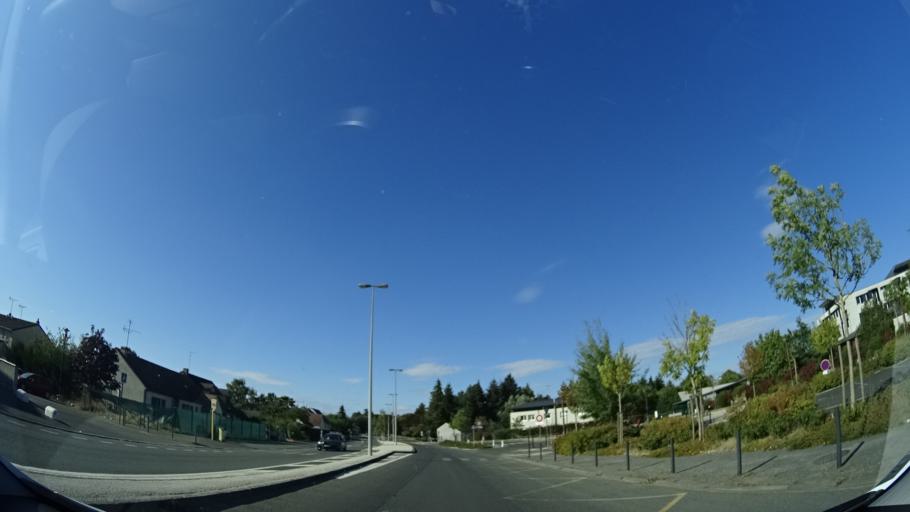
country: FR
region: Centre
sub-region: Departement du Loiret
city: Saint-Jean-de-Braye
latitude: 47.9128
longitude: 1.9783
